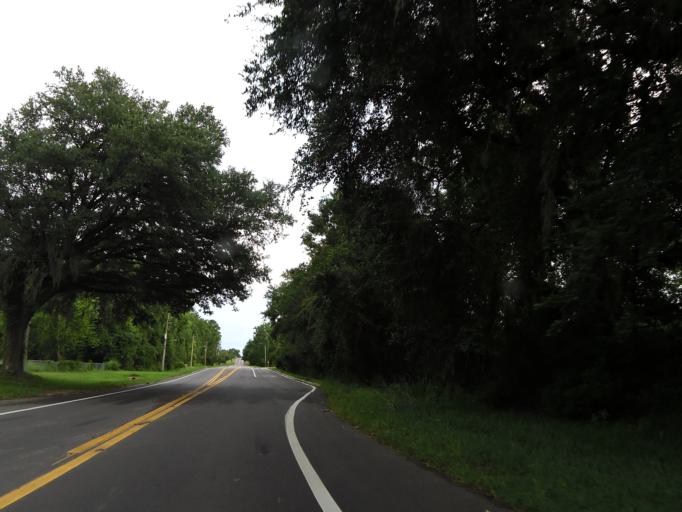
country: US
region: Florida
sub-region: Nassau County
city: Nassau Village-Ratliff
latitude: 30.4081
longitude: -81.7573
